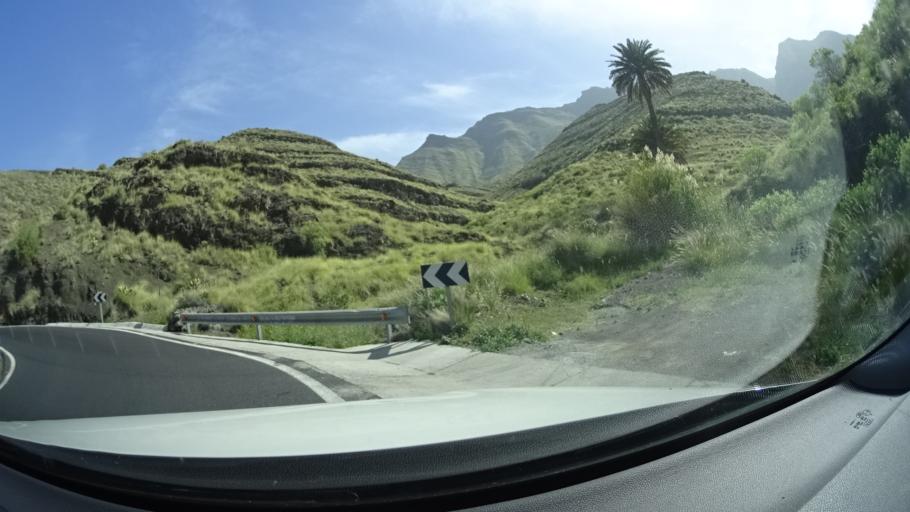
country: ES
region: Canary Islands
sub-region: Provincia de Las Palmas
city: Agaete
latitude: 28.0808
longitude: -15.7050
